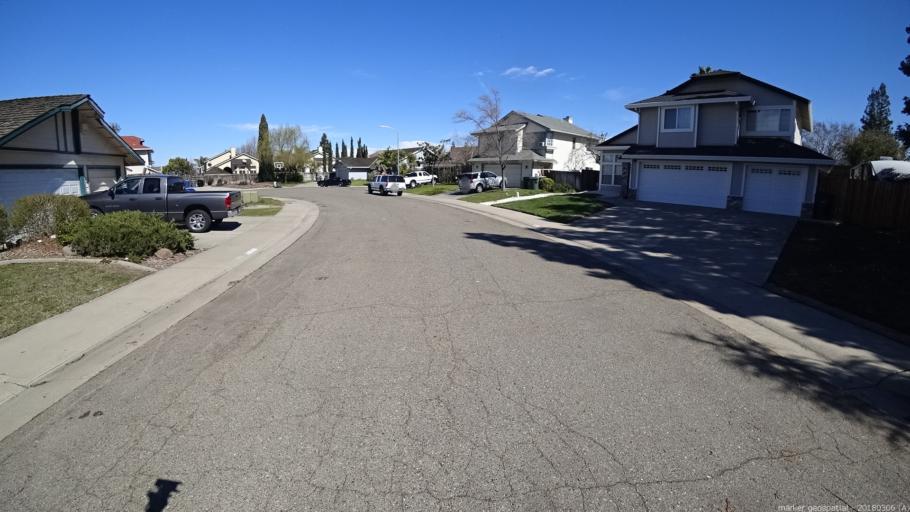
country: US
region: California
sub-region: Sacramento County
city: Vineyard
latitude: 38.4661
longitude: -121.3612
